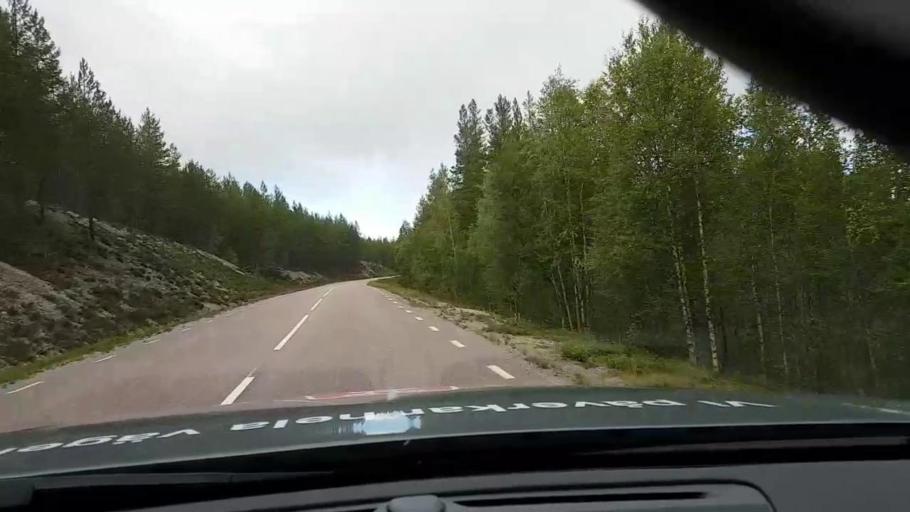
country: SE
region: Vaesterbotten
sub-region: Asele Kommun
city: Asele
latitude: 63.8790
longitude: 17.3558
